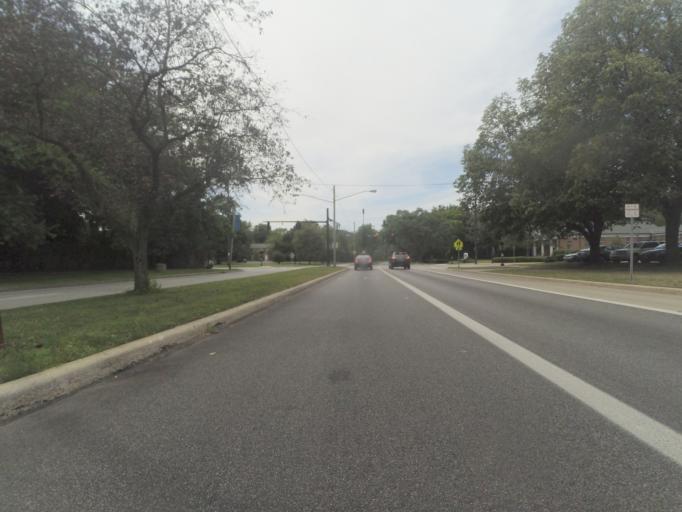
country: US
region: Ohio
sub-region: Cuyahoga County
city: University Heights
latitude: 41.4866
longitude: -81.5644
